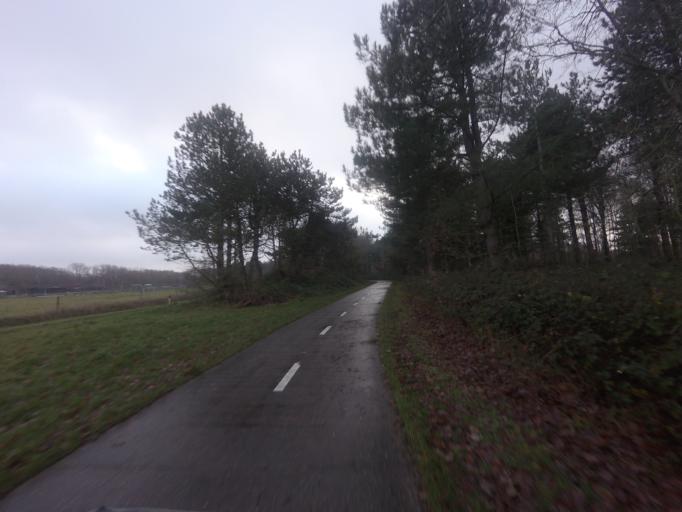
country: NL
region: North Holland
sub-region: Gemeente Texel
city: Den Burg
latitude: 53.1538
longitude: 4.8632
